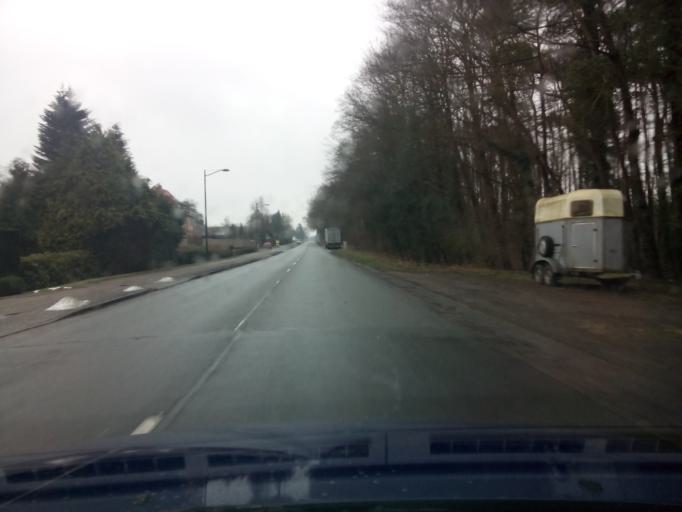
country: DE
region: Lower Saxony
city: Hambergen
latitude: 53.3148
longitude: 8.8617
